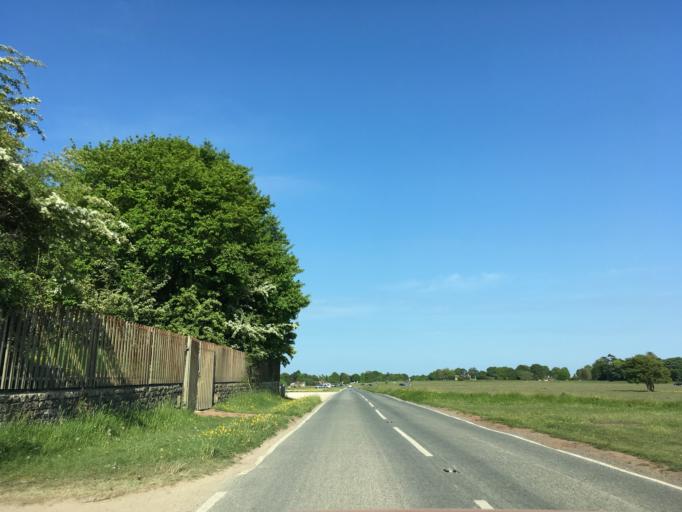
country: GB
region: England
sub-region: Gloucestershire
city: Nailsworth
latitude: 51.7096
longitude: -2.2116
